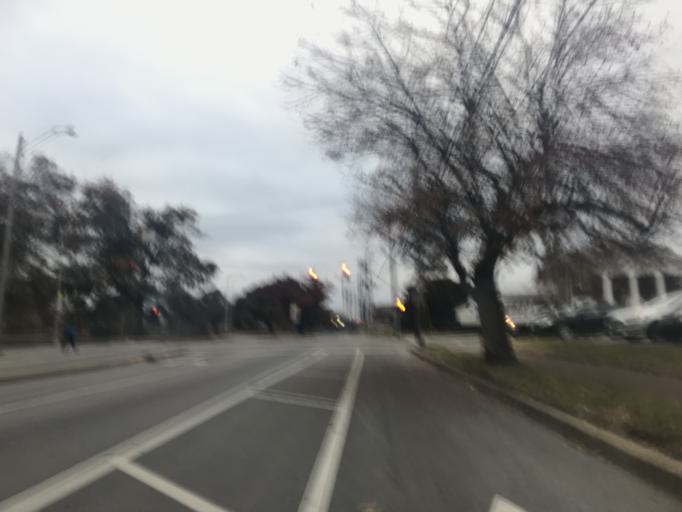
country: US
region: Kentucky
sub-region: Jefferson County
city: Louisville
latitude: 38.2509
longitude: -85.7729
